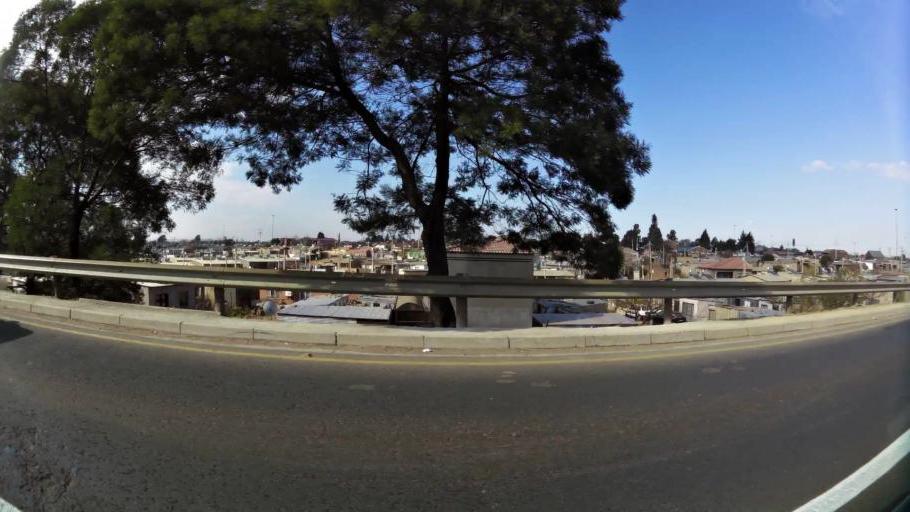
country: ZA
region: Gauteng
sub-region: City of Johannesburg Metropolitan Municipality
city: Soweto
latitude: -26.2696
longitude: 27.8903
